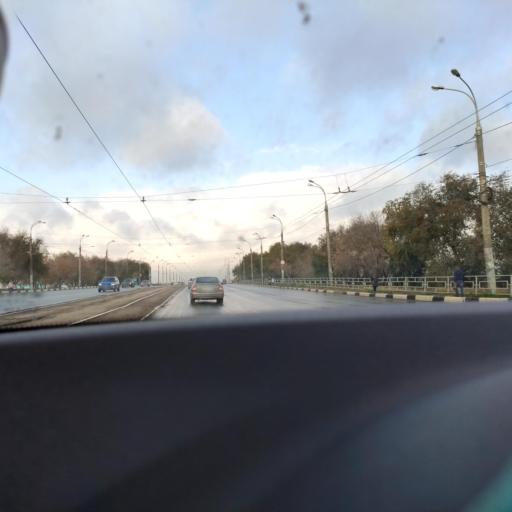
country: RU
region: Samara
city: Smyshlyayevka
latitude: 53.2107
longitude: 50.2733
